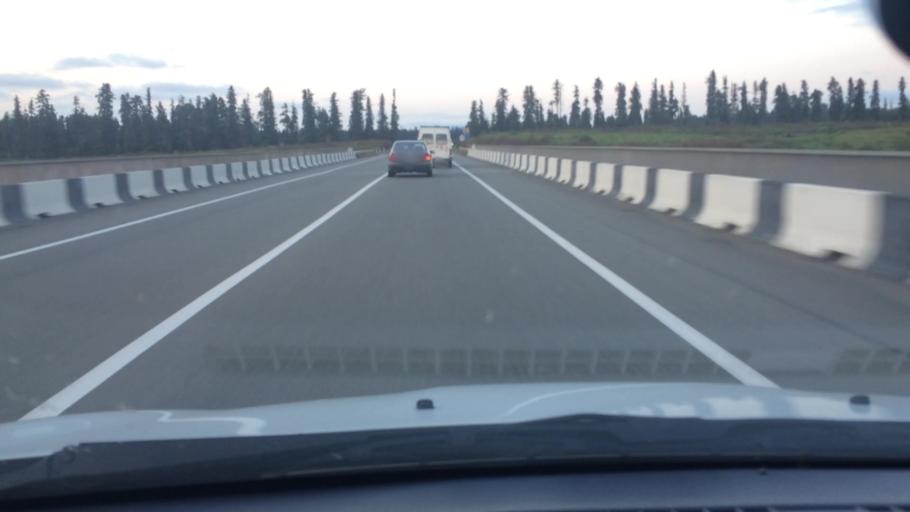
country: GE
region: Ajaria
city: Ochkhamuri
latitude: 41.8365
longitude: 41.8247
